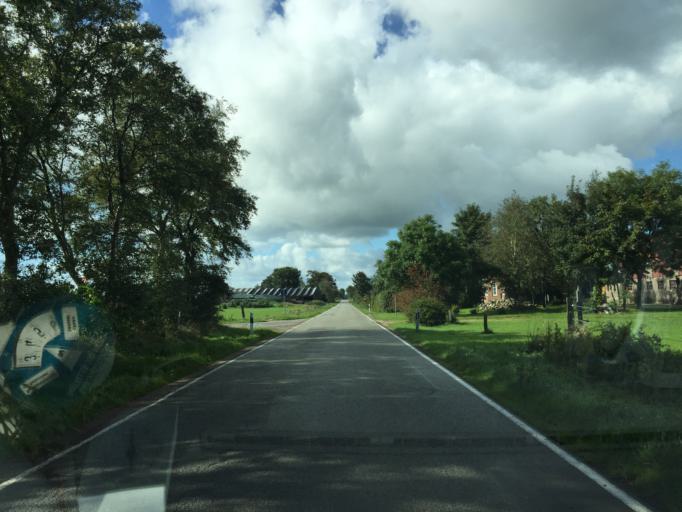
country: DE
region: Schleswig-Holstein
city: Bramstedtlund
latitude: 54.8388
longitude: 9.0646
